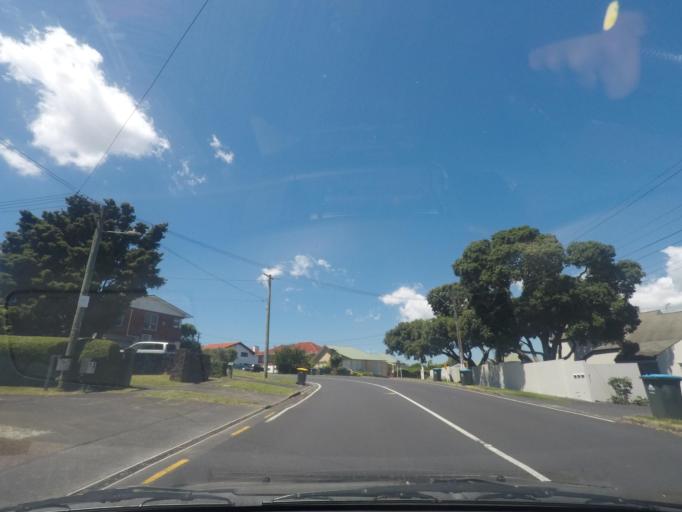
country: NZ
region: Auckland
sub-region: Auckland
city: Auckland
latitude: -36.9114
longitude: 174.7573
